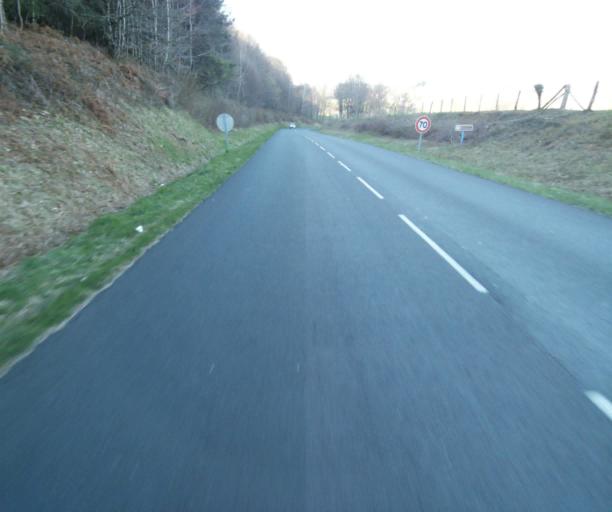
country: FR
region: Limousin
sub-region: Departement de la Correze
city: Seilhac
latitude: 45.3551
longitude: 1.7084
